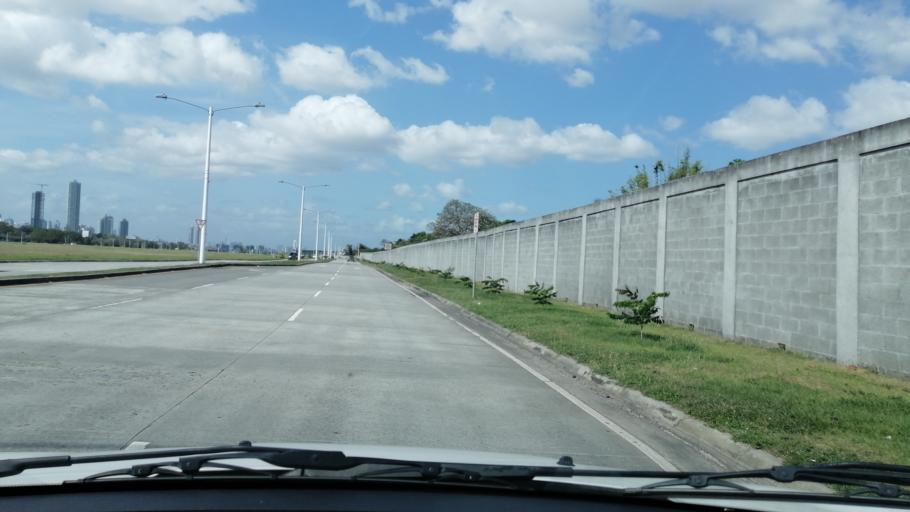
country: PA
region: Panama
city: San Miguelito
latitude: 9.0399
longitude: -79.4256
